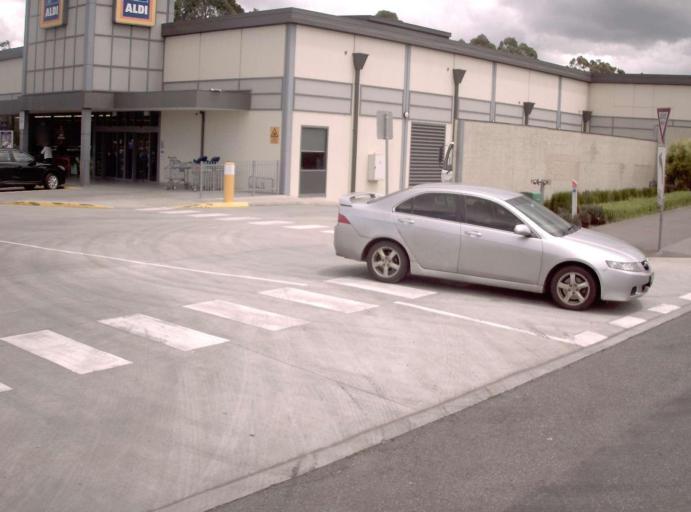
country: AU
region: Victoria
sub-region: Baw Baw
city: Warragul
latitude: -38.1626
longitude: 145.9276
